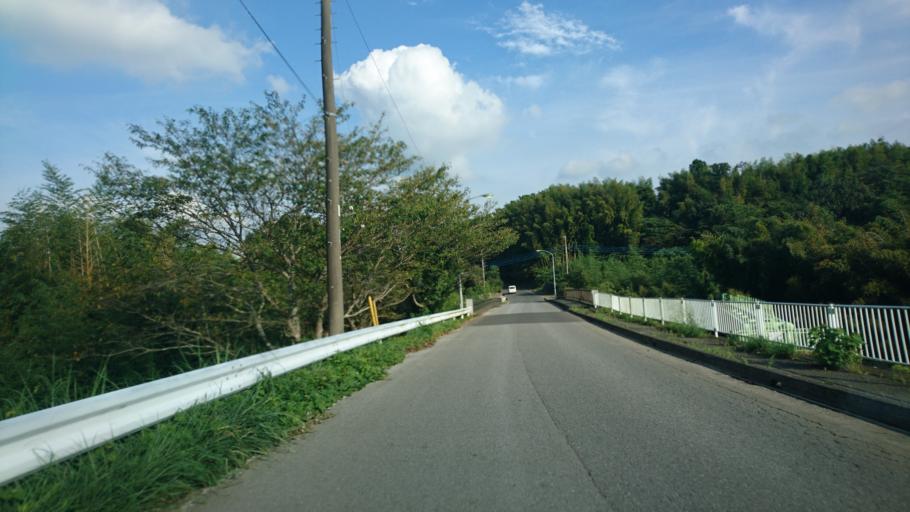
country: JP
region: Chiba
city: Kimitsu
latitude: 35.2799
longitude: 139.9865
